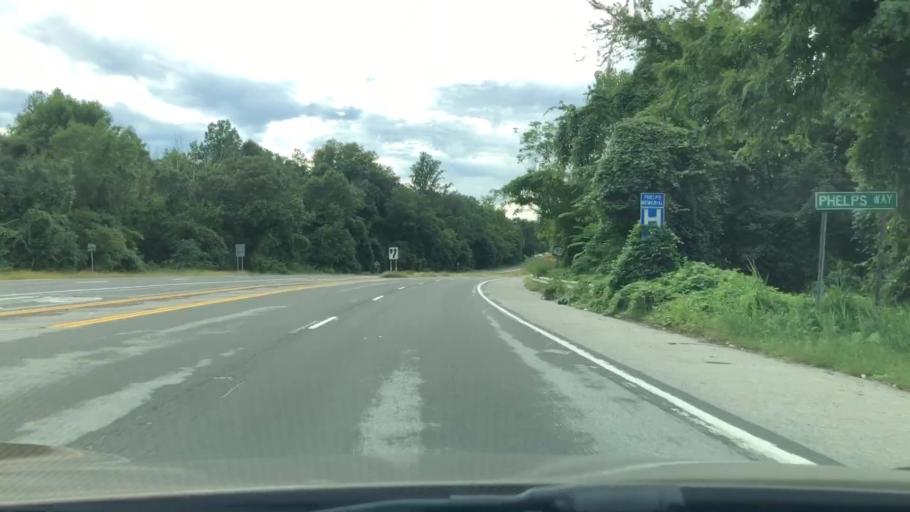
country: US
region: New York
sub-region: Westchester County
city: Hawthorne
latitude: 41.1219
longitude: -73.8159
